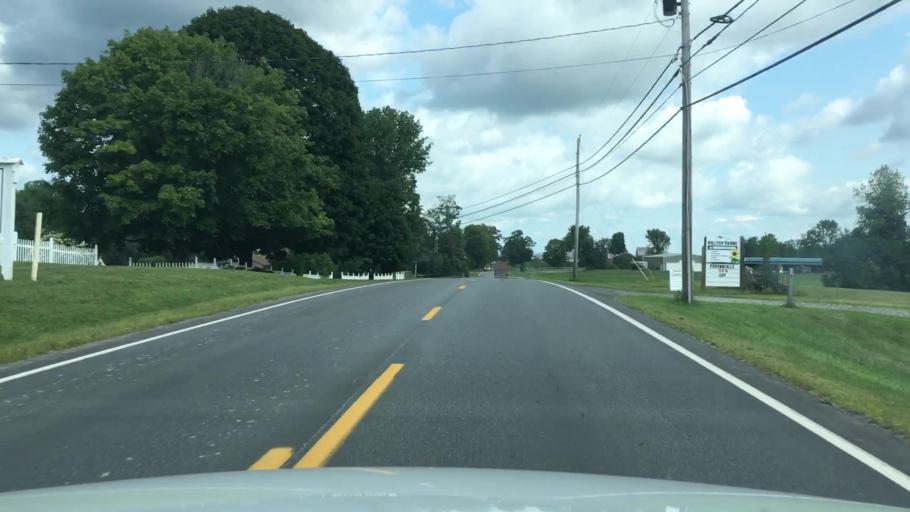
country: US
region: Maine
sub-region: Somerset County
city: Fairfield
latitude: 44.6388
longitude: -69.6791
